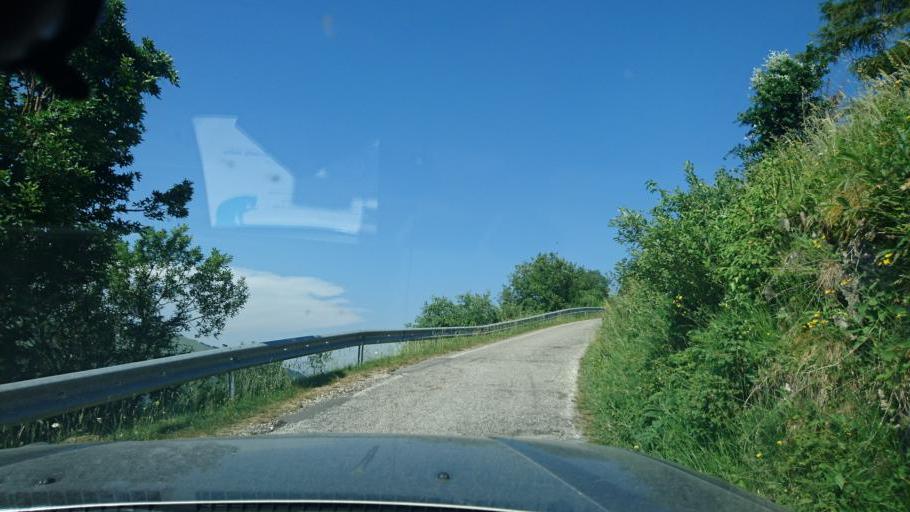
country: IT
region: Veneto
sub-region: Provincia di Treviso
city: Crespano del Grappa
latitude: 45.8939
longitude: 11.8295
